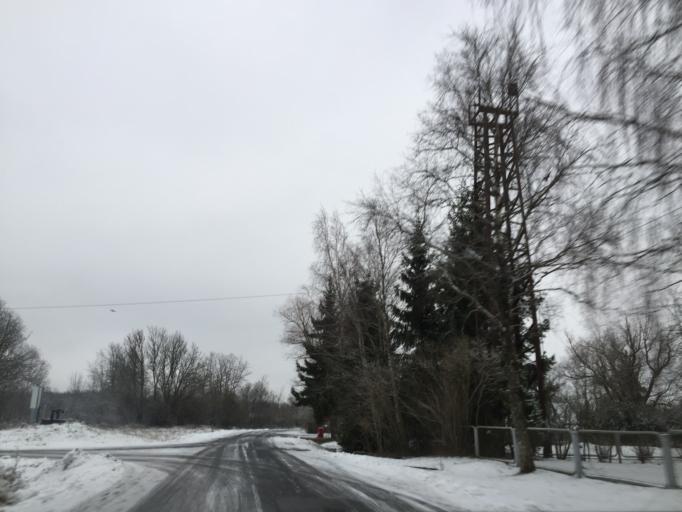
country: EE
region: Laeaene
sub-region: Lihula vald
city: Lihula
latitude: 58.6809
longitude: 23.8372
